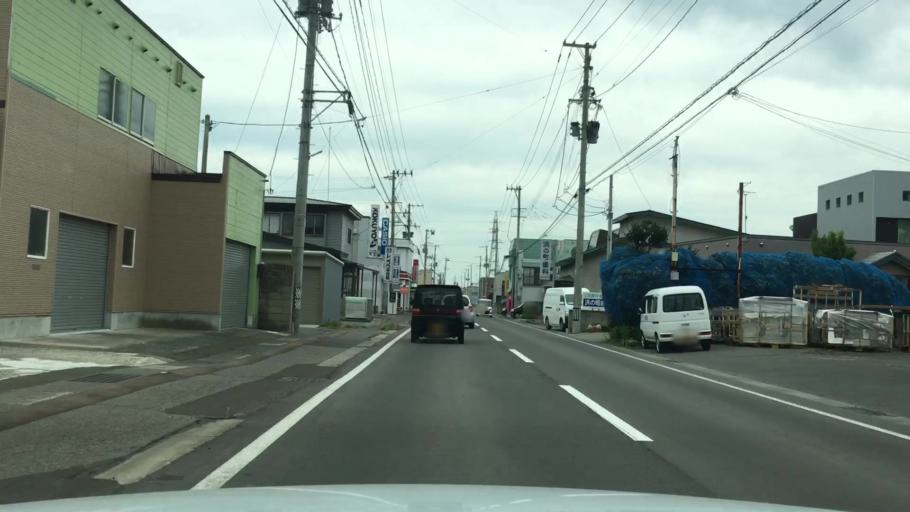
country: JP
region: Aomori
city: Hirosaki
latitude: 40.6240
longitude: 140.4567
